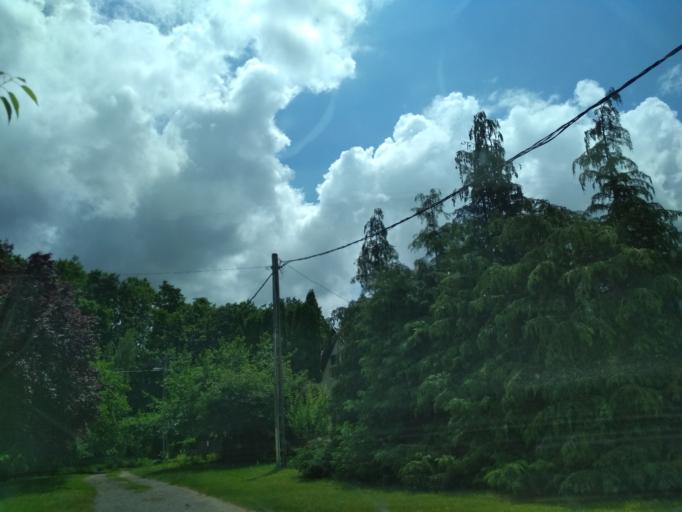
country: HU
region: Jasz-Nagykun-Szolnok
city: Tiszafured
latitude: 47.6187
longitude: 20.7293
